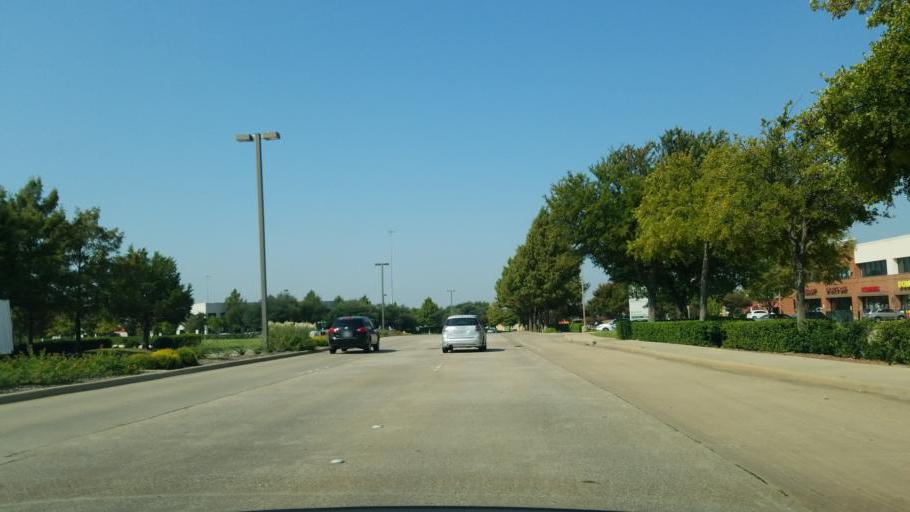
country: US
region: Texas
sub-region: Collin County
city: Allen
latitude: 33.0914
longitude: -96.6778
